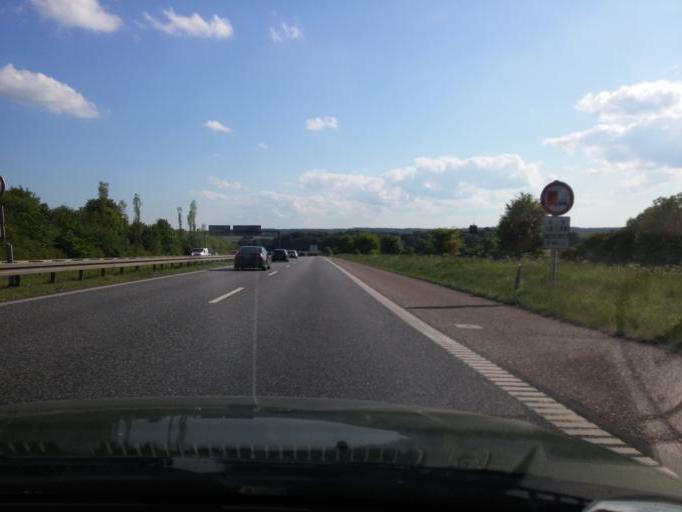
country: DK
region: South Denmark
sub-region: Kolding Kommune
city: Kolding
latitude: 55.5073
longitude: 9.4266
